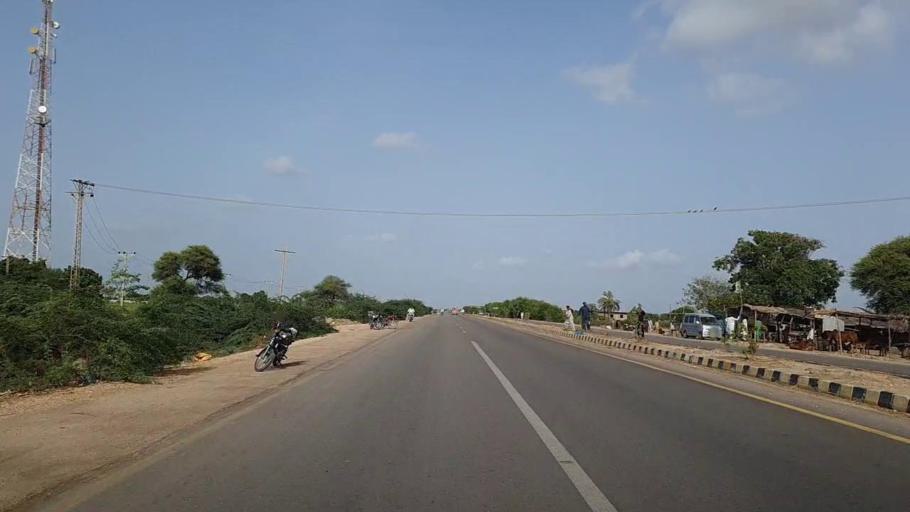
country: PK
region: Sindh
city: Thatta
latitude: 24.7430
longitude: 67.7730
